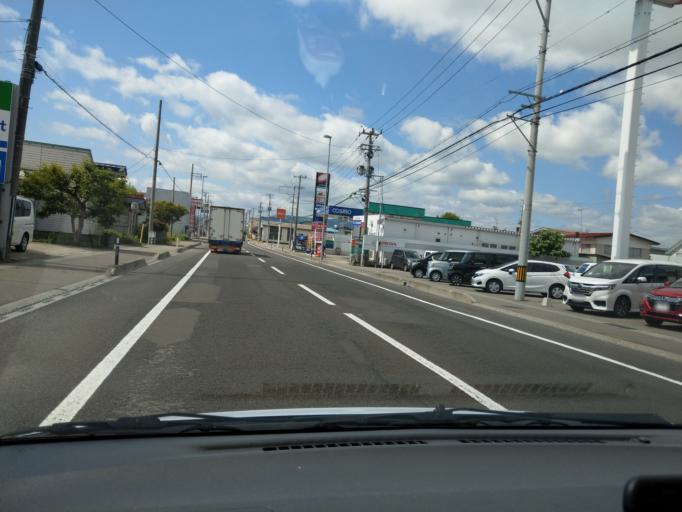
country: JP
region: Akita
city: Yuzawa
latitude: 39.1758
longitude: 140.4924
